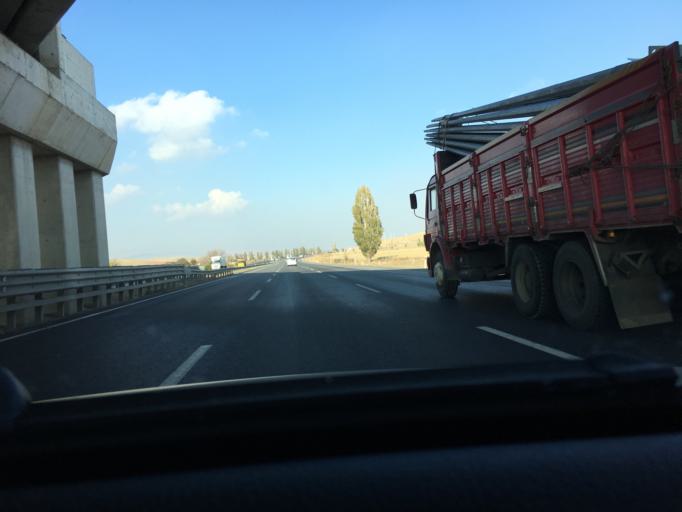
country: TR
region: Ankara
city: Polatli
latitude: 39.6241
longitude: 32.1921
